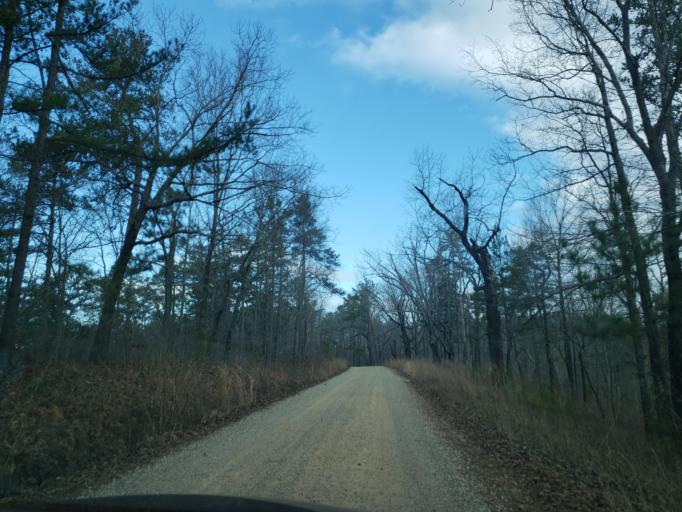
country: US
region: Alabama
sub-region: Cleburne County
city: Heflin
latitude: 33.6697
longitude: -85.6353
